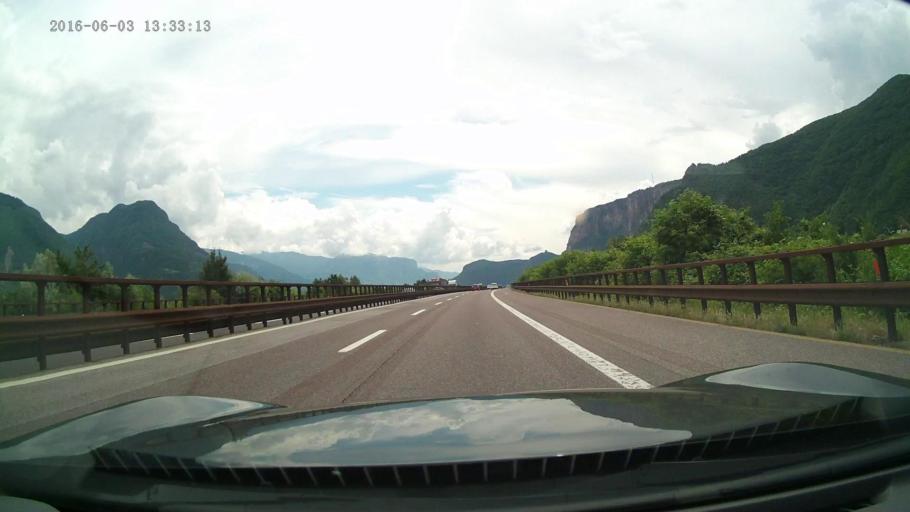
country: IT
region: Trentino-Alto Adige
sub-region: Bolzano
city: Vadena
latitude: 46.4228
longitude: 11.3142
